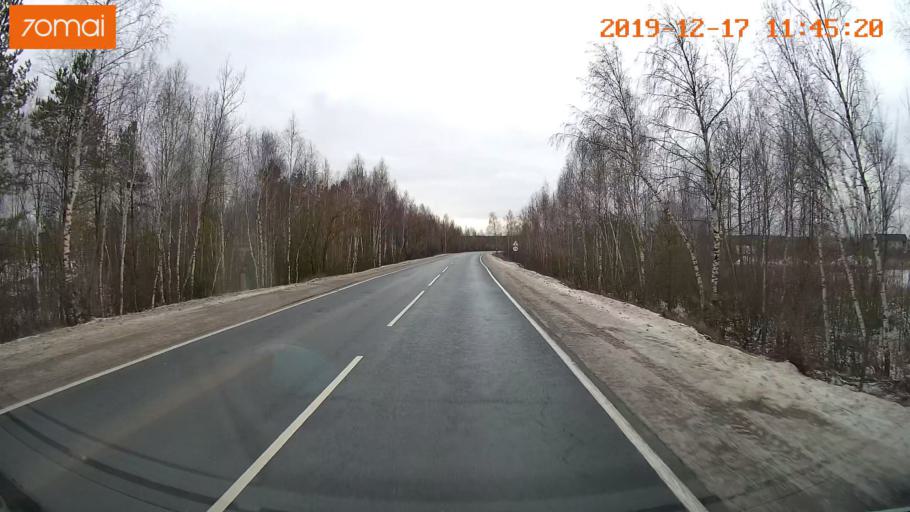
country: RU
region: Vladimir
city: Velikodvorskiy
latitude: 55.2518
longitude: 40.6724
